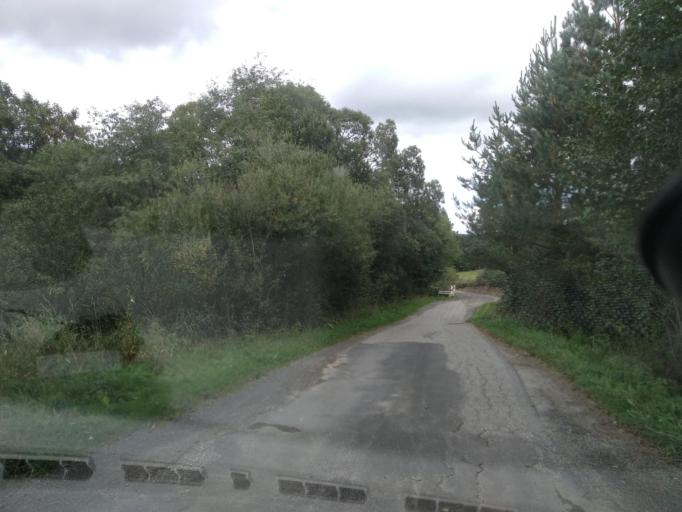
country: PL
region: Lesser Poland Voivodeship
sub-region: Powiat gorlicki
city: Uscie Gorlickie
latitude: 49.5289
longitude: 21.1651
